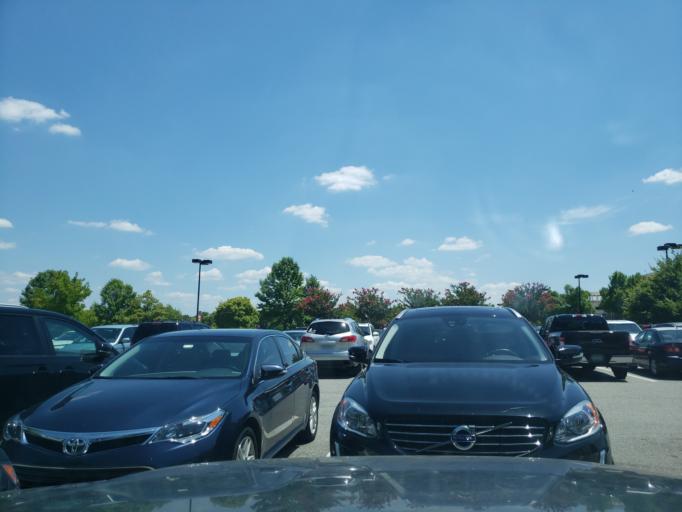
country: US
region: North Carolina
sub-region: Orange County
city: Chapel Hill
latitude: 35.9037
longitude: -78.9564
